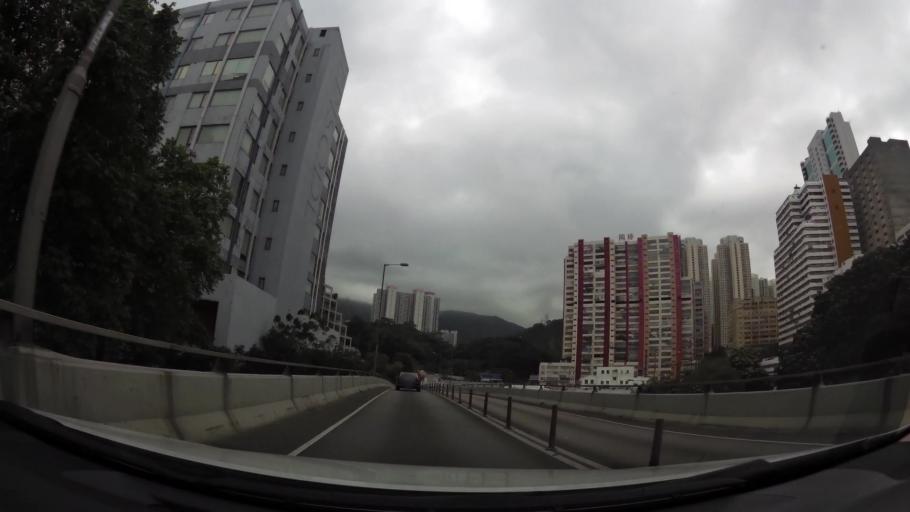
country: HK
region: Tsuen Wan
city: Tsuen Wan
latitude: 22.3693
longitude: 114.1342
